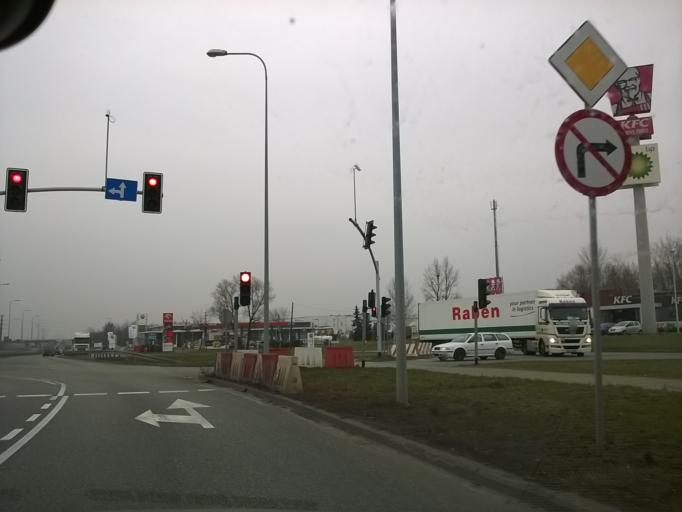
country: PL
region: Silesian Voivodeship
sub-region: Powiat gliwicki
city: Przyszowice
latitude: 50.2675
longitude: 18.7121
